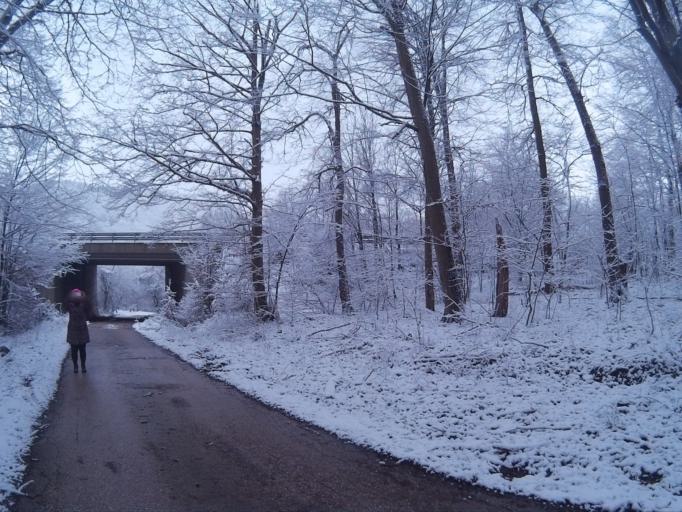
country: HU
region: Komarom-Esztergom
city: Tarjan
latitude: 47.5767
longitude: 18.4574
